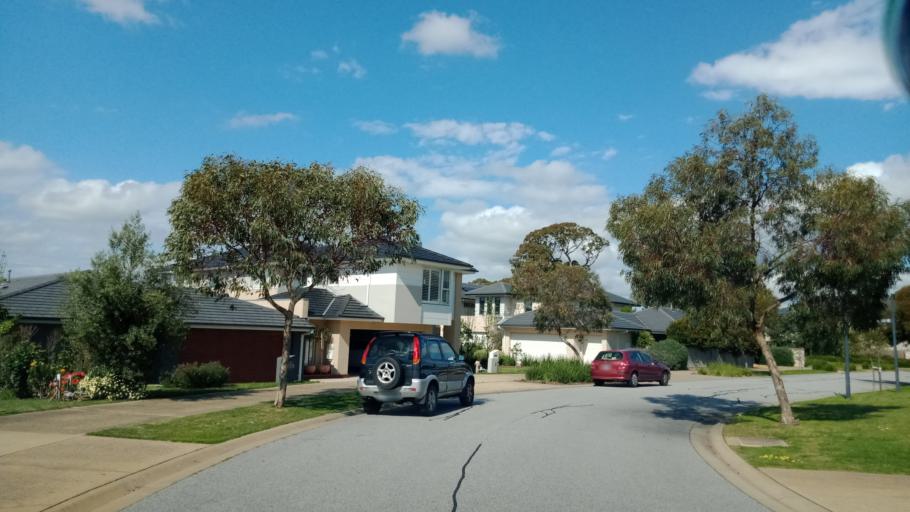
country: AU
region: Victoria
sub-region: Frankston
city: Sandhurst
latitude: -38.0846
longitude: 145.2110
